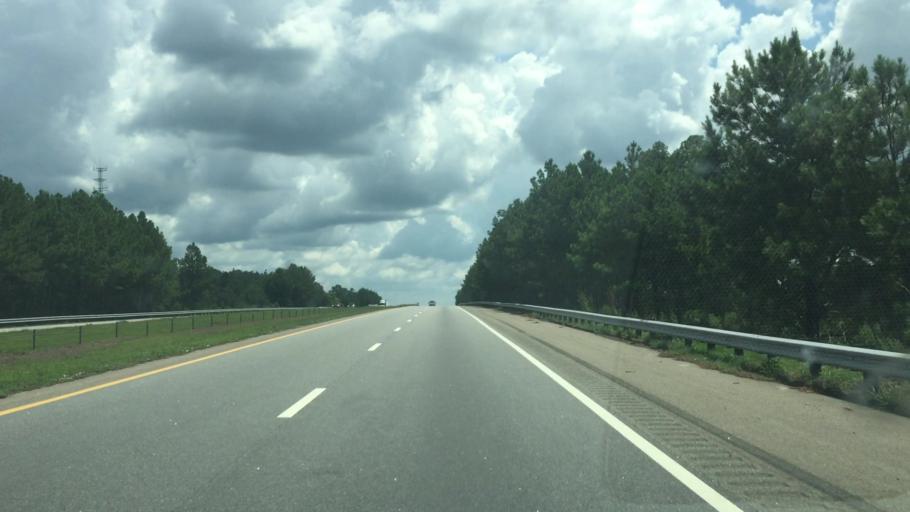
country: US
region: North Carolina
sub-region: Richmond County
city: Hamlet
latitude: 34.8678
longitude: -79.6557
